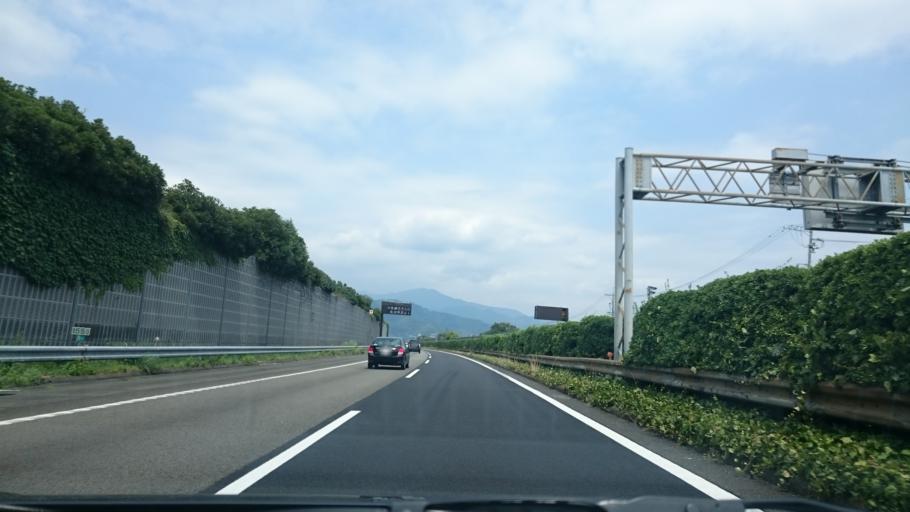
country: JP
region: Shizuoka
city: Shizuoka-shi
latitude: 34.9890
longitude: 138.4357
